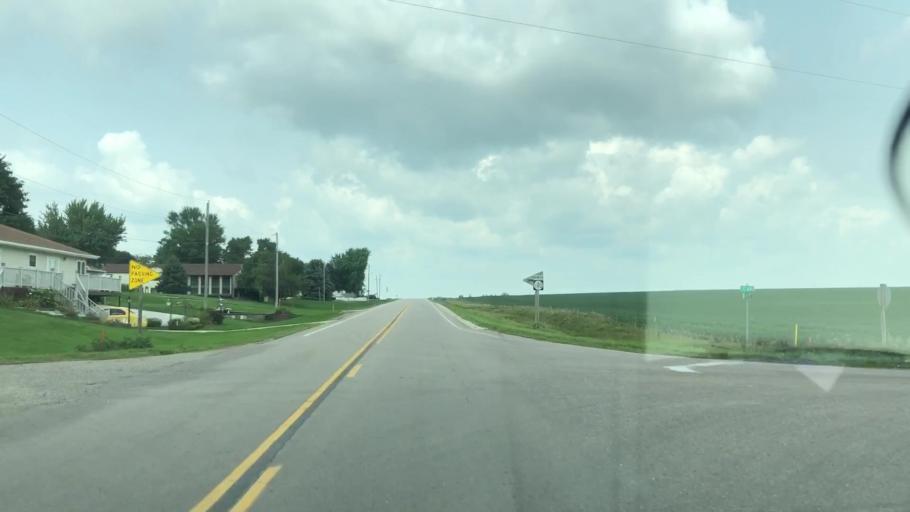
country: US
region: Iowa
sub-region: Plymouth County
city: Kingsley
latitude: 42.5899
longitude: -95.9574
